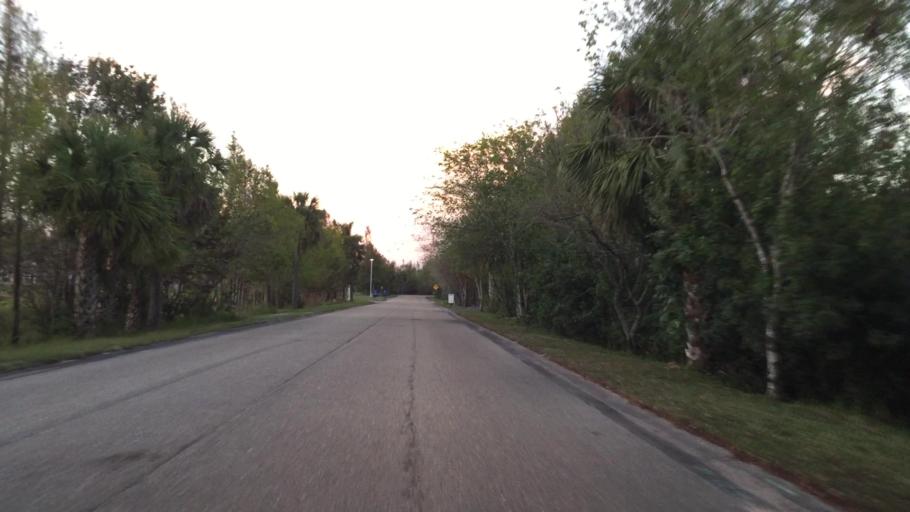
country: US
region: Florida
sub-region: Lee County
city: Gateway
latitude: 26.5361
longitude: -81.7915
